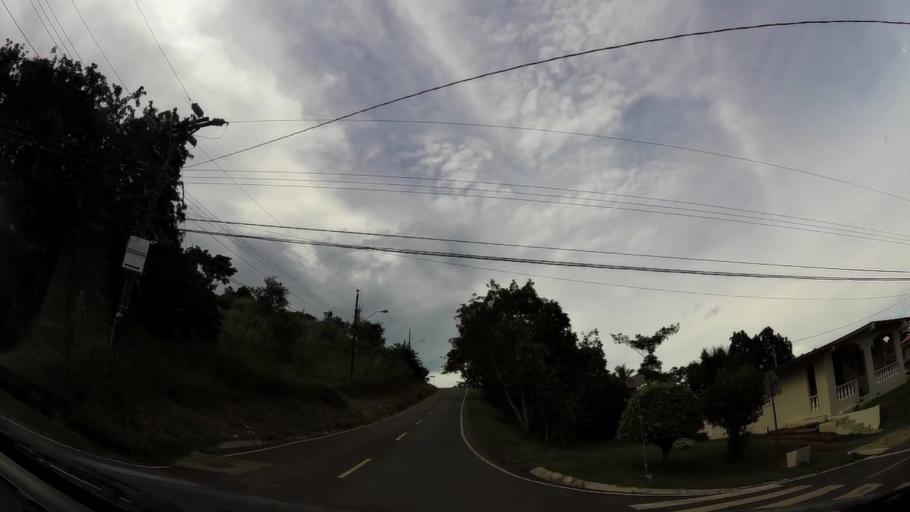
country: PA
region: Panama
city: Guadalupe
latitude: 8.8565
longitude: -79.8126
